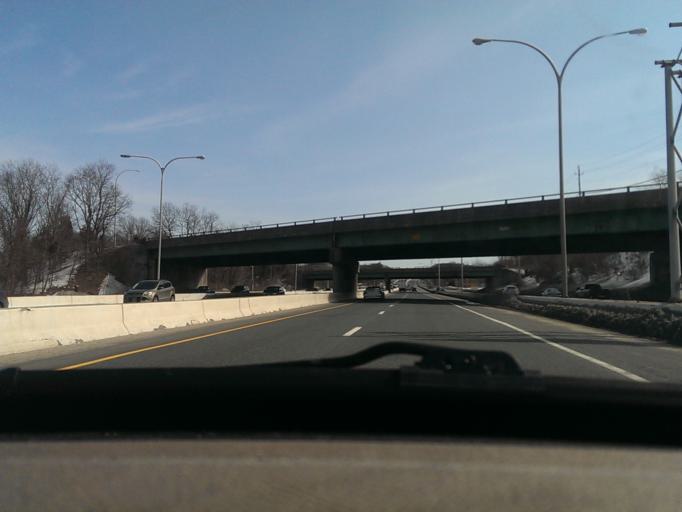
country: US
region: Rhode Island
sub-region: Providence County
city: Cumberland Hill
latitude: 41.9444
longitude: -71.4778
